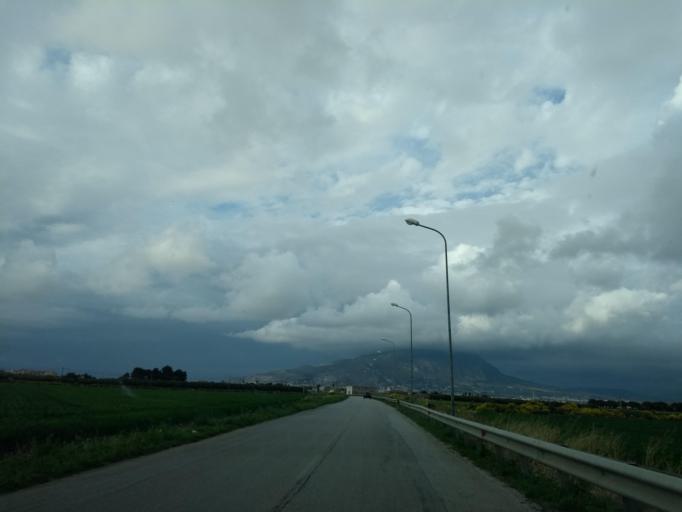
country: IT
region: Sicily
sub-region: Trapani
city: Paceco
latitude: 37.9759
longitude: 12.5275
